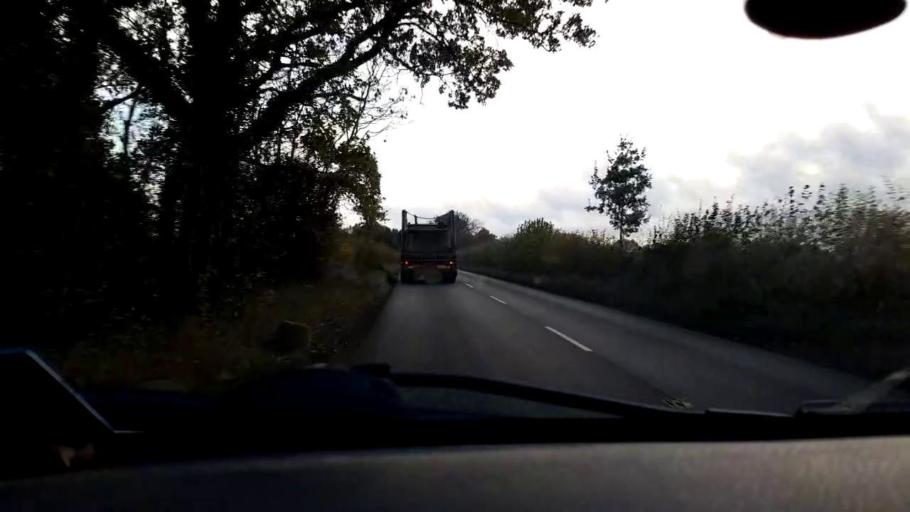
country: GB
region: England
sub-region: Norfolk
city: Mattishall
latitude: 52.6857
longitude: 1.1016
